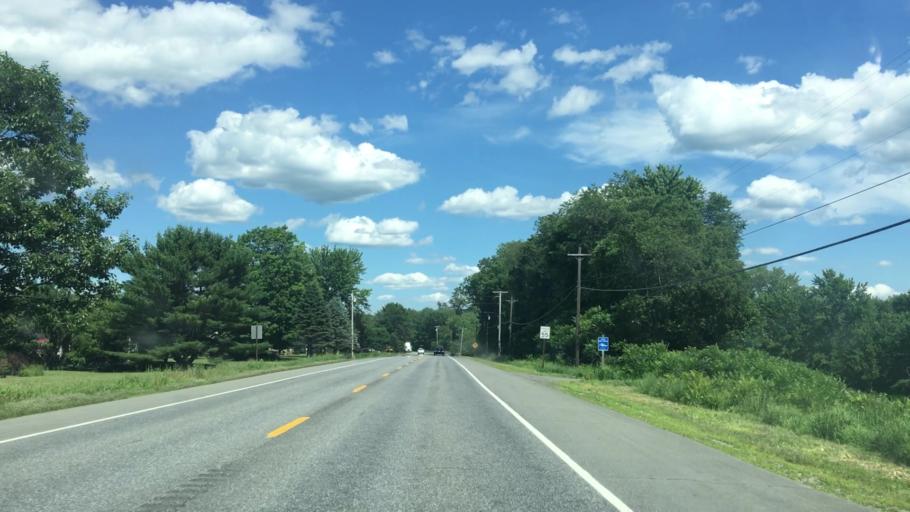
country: US
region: Maine
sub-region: Franklin County
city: New Sharon
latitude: 44.6214
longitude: -70.0661
